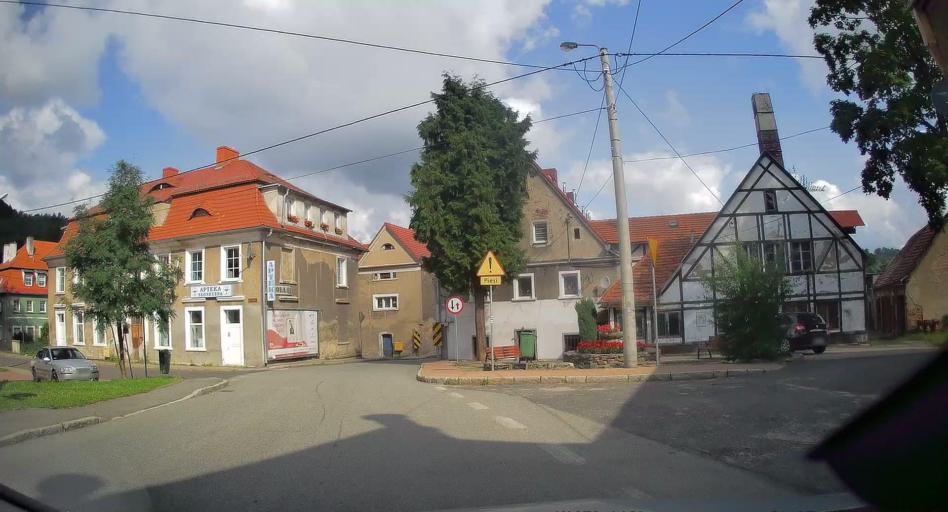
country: PL
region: Lower Silesian Voivodeship
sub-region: Powiat walbrzyski
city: Walim
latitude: 50.6999
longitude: 16.4407
